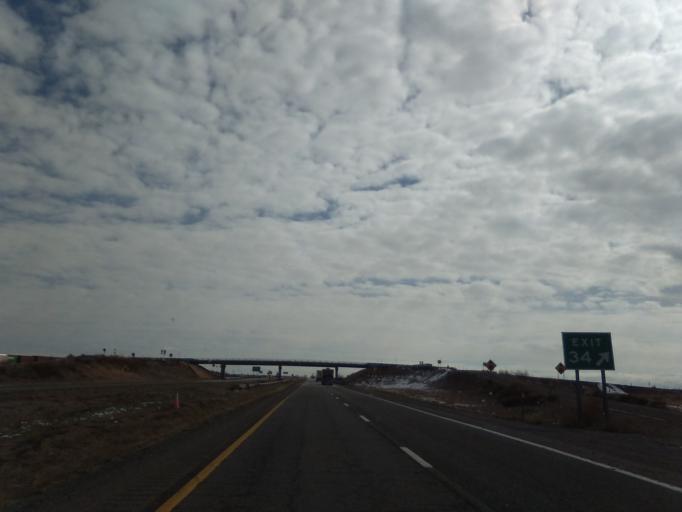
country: US
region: New Mexico
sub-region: Hidalgo County
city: Lordsburg
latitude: 32.2712
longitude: -108.5381
